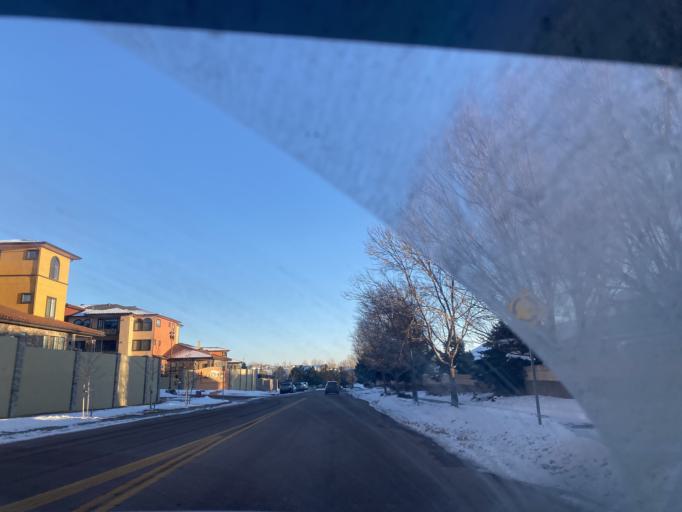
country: US
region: Colorado
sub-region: El Paso County
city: Black Forest
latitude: 38.9658
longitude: -104.7453
